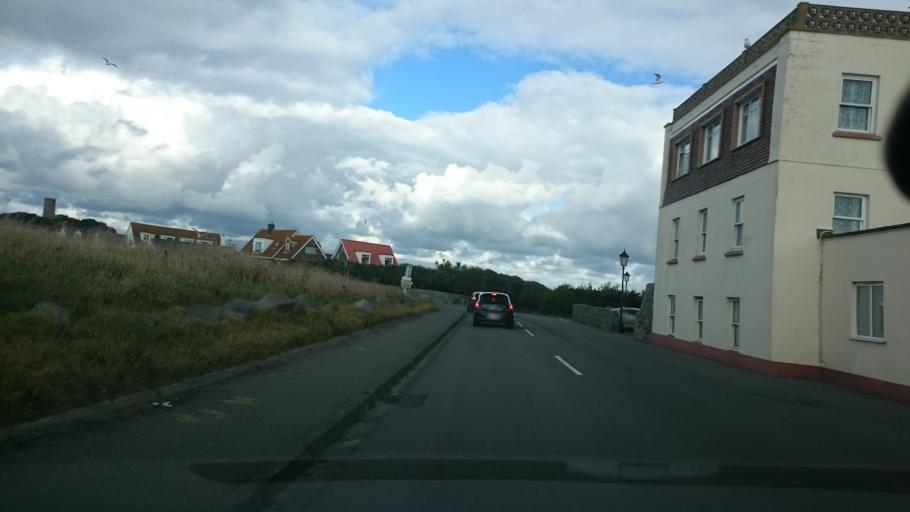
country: GG
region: St Peter Port
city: Saint Peter Port
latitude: 49.4531
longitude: -2.6503
